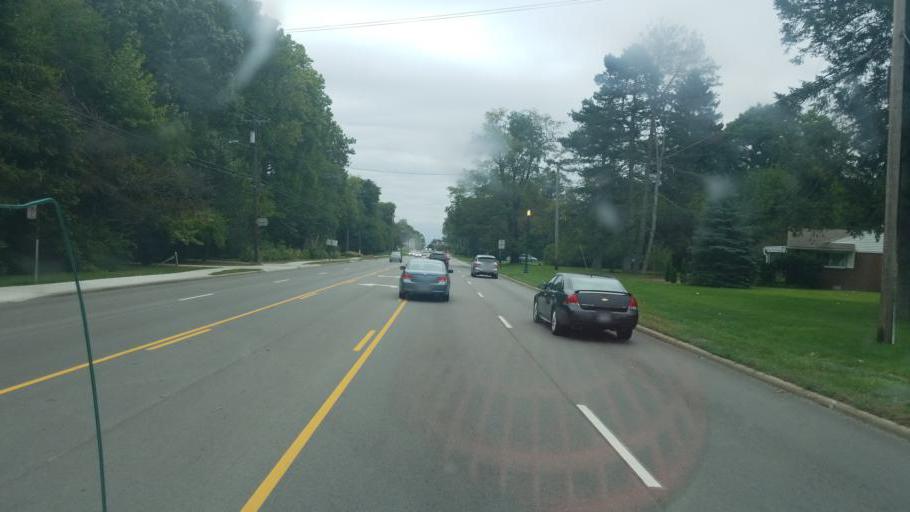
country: US
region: Ohio
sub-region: Lucas County
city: Ottawa Hills
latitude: 41.6770
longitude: -83.6508
